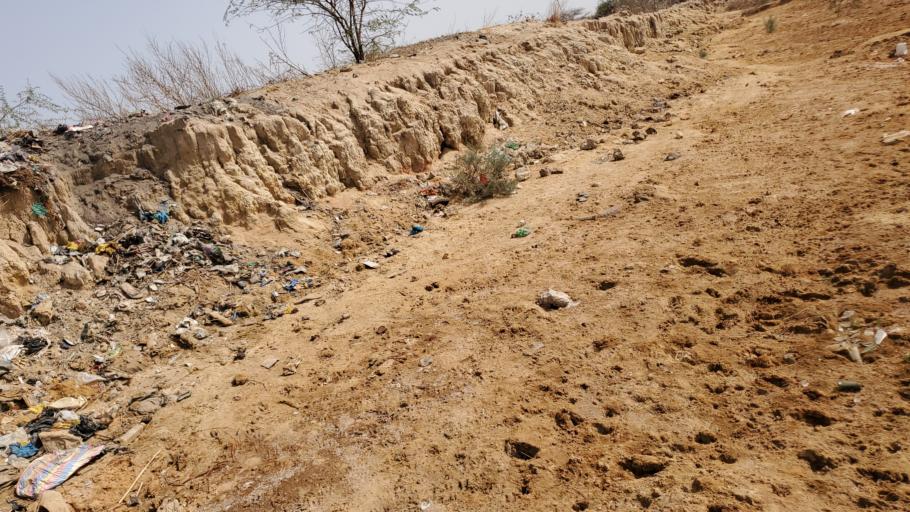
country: SN
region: Saint-Louis
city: Saint-Louis
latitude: 15.9494
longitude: -16.4304
